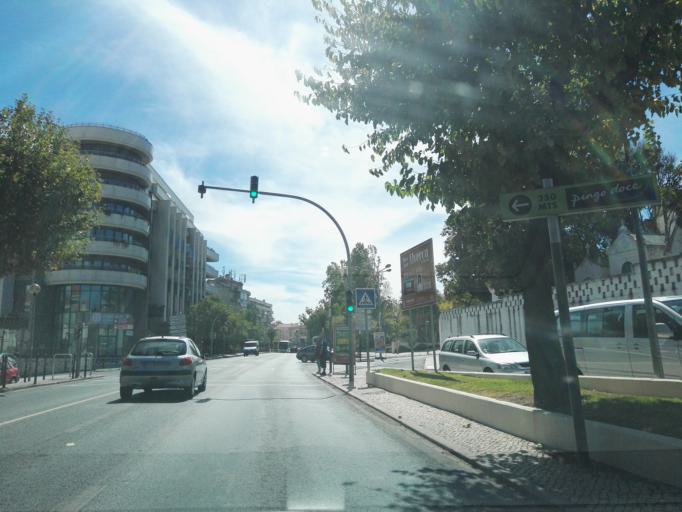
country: PT
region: Lisbon
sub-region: Vila Franca de Xira
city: Sobralinho
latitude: 38.8971
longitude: -9.0385
